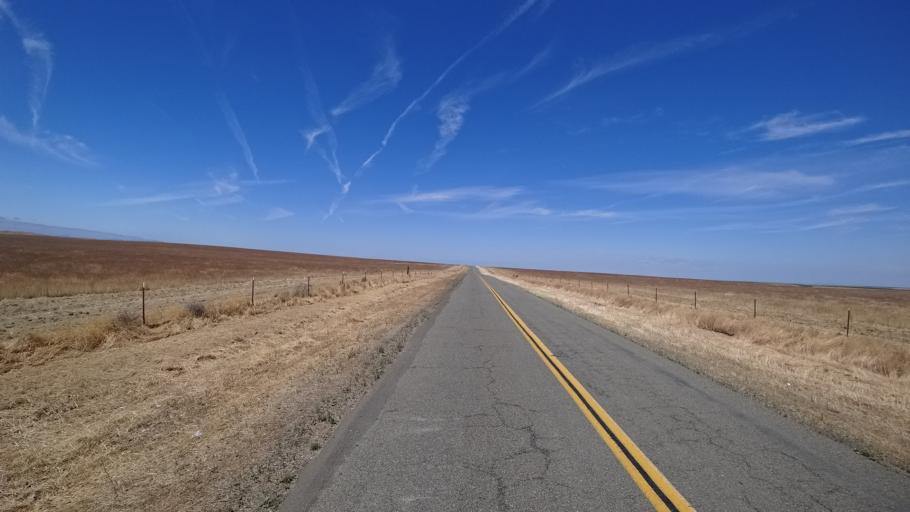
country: US
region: California
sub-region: Kings County
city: Kettleman City
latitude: 35.7978
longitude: -119.8941
